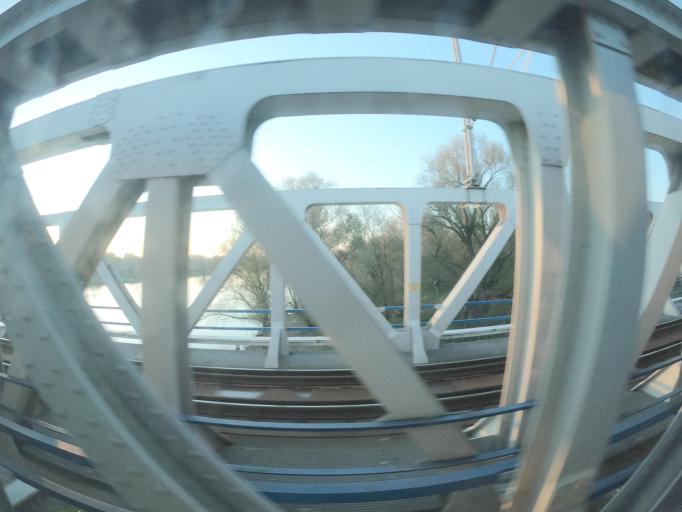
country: PL
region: Lubusz
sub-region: Powiat gorzowski
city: Kostrzyn nad Odra
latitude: 52.5852
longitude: 14.6439
